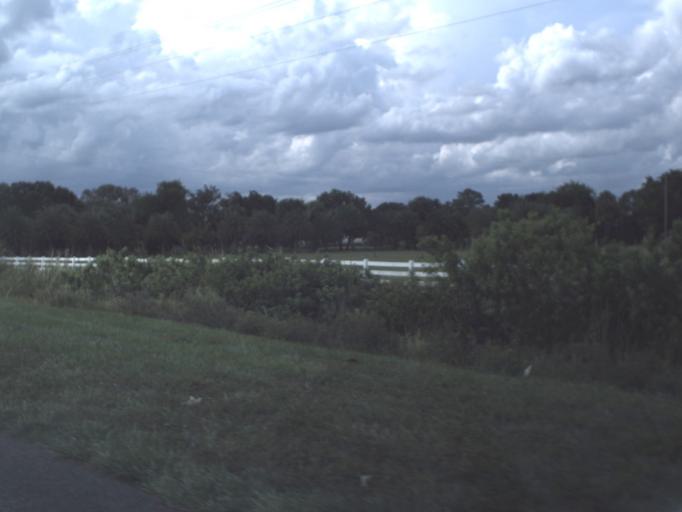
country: US
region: Florida
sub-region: Hendry County
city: Harlem
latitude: 26.7544
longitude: -80.9895
